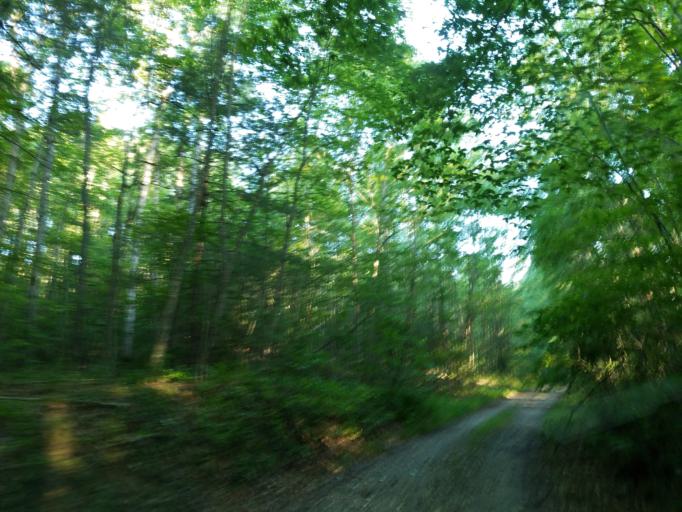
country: US
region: Georgia
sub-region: Fannin County
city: Blue Ridge
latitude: 34.8149
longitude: -84.1434
